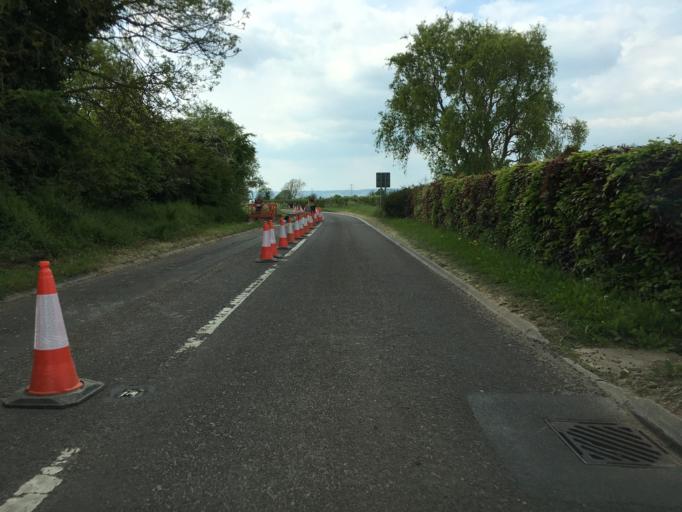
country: GB
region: England
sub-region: South Gloucestershire
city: Thornbury
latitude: 51.6232
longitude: -2.5219
